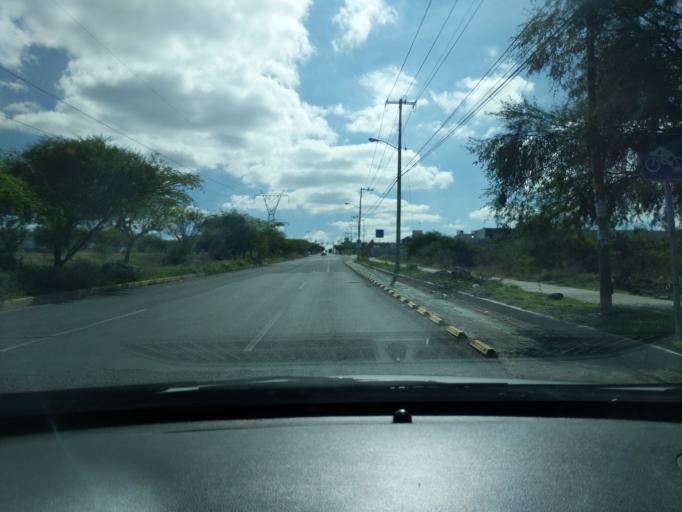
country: MX
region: Queretaro
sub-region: Queretaro
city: Patria Nueva
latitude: 20.6409
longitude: -100.4946
